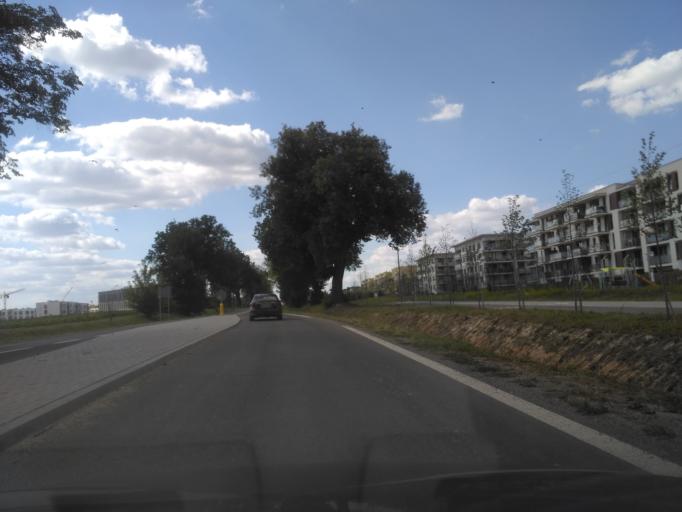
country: PL
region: Lublin Voivodeship
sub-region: Powiat lubelski
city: Jakubowice Murowane
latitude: 51.2155
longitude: 22.6351
